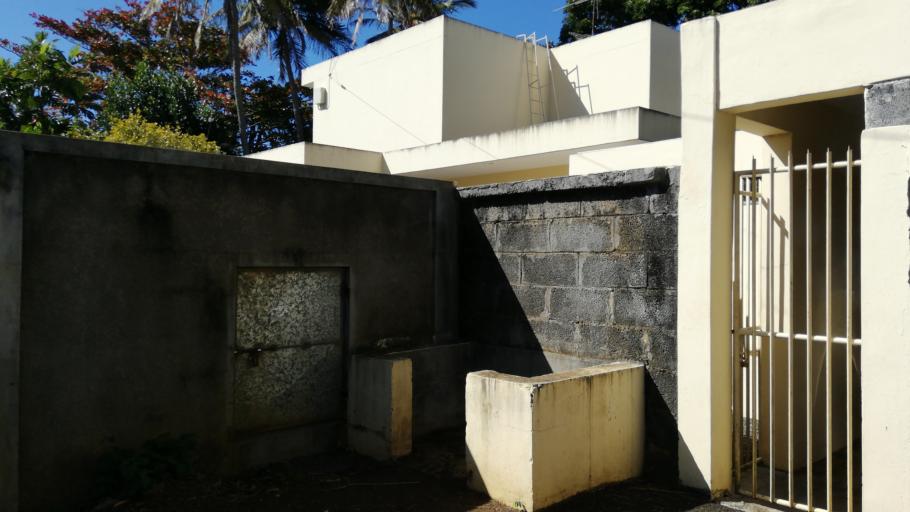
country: MU
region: Plaines Wilhems
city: Ebene
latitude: -20.2374
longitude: 57.4771
